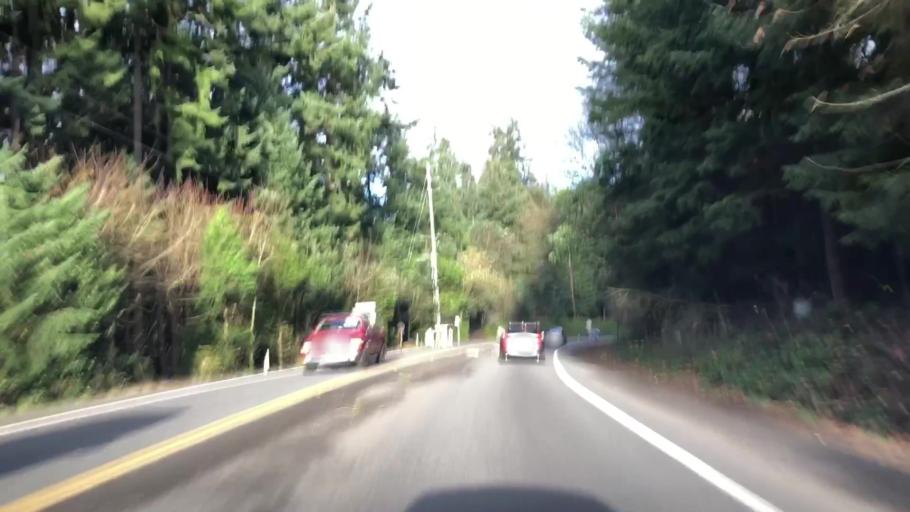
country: US
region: Washington
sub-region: Kitsap County
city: Suquamish
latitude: 47.7051
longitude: -122.5600
